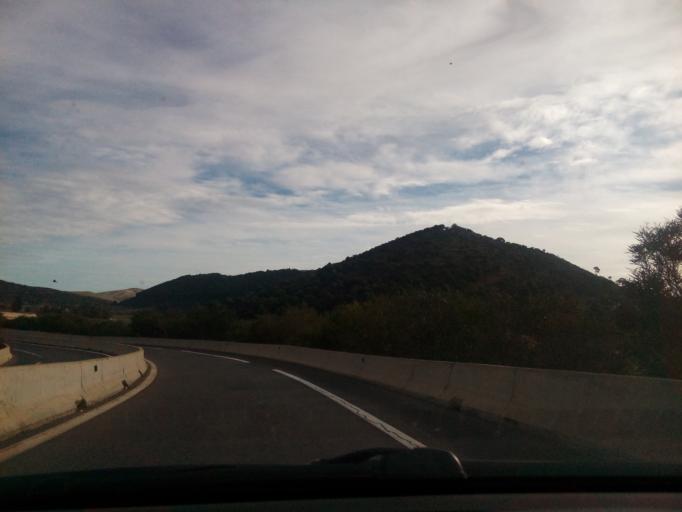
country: DZ
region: Sidi Bel Abbes
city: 'Ain el Berd
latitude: 35.3811
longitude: -0.5000
